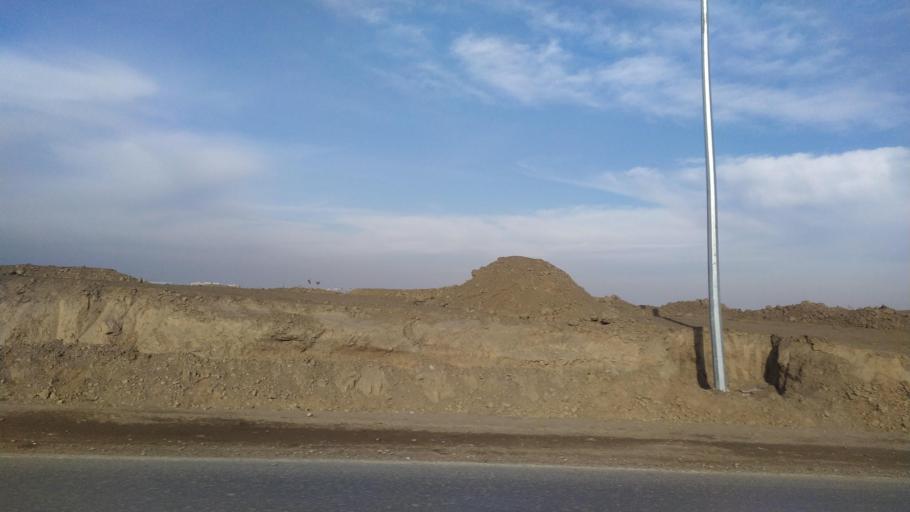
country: KZ
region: Almaty Oblysy
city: Burunday
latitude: 43.2241
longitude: 76.7264
